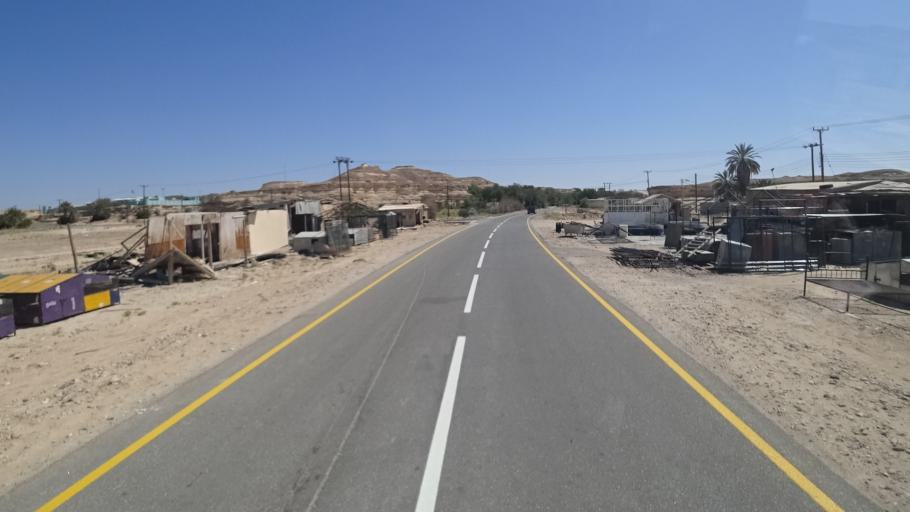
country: OM
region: Zufar
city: Salalah
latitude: 17.4807
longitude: 53.3509
